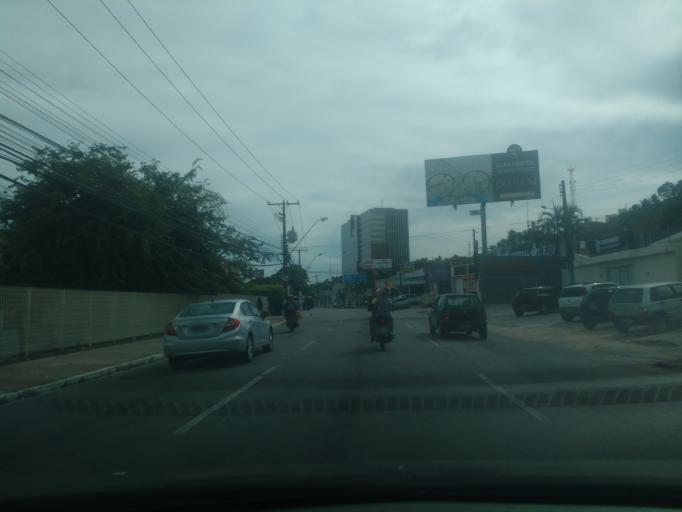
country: BR
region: Alagoas
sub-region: Maceio
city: Maceio
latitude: -9.6471
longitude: -35.7154
